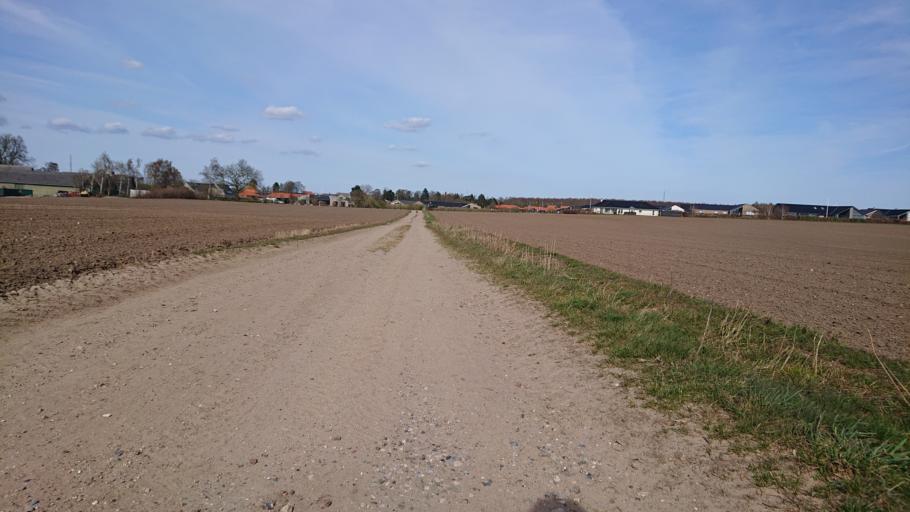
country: DK
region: South Denmark
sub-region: Nyborg Kommune
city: Nyborg
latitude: 55.3043
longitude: 10.7490
